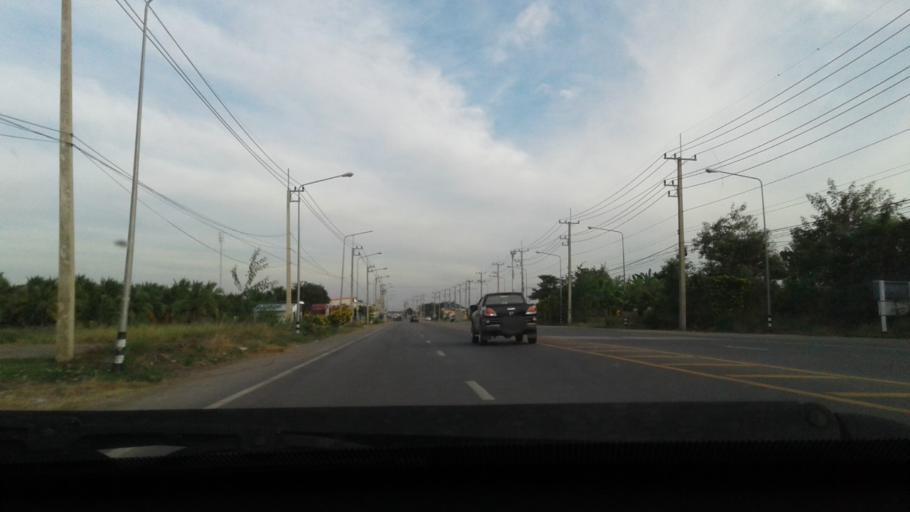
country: TH
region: Nonthaburi
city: Sai Noi
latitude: 13.9267
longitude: 100.2490
